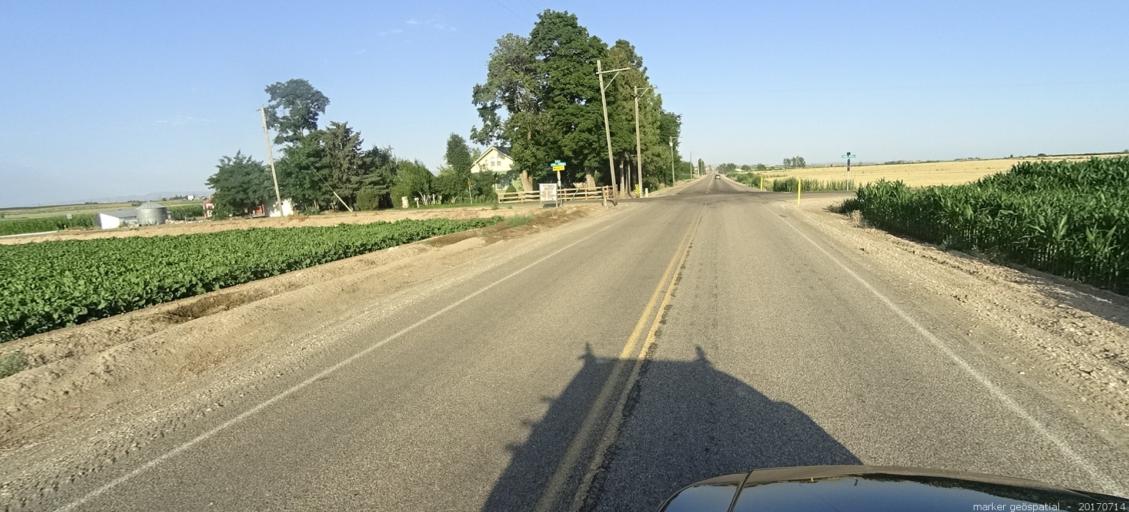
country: US
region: Idaho
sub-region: Canyon County
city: Nampa
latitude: 43.4593
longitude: -116.5128
